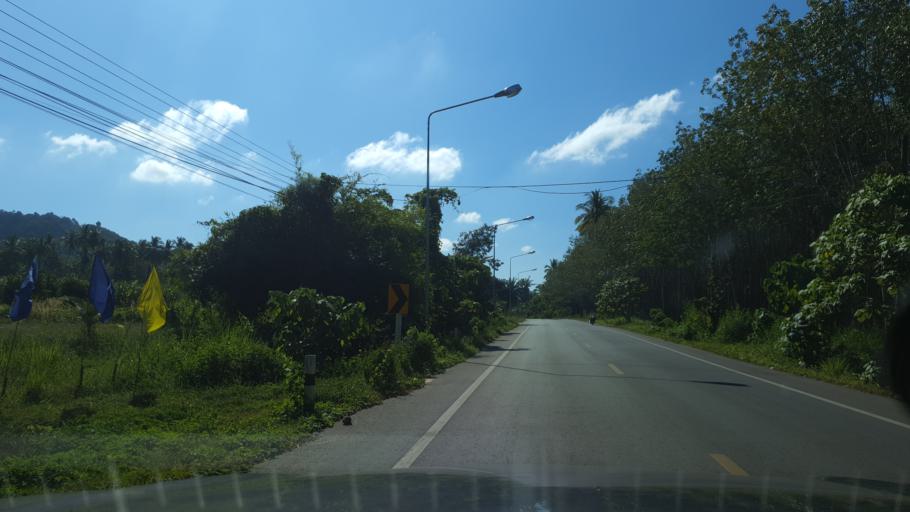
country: TH
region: Phangnga
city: Ban Ao Nang
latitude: 8.0735
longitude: 98.8067
